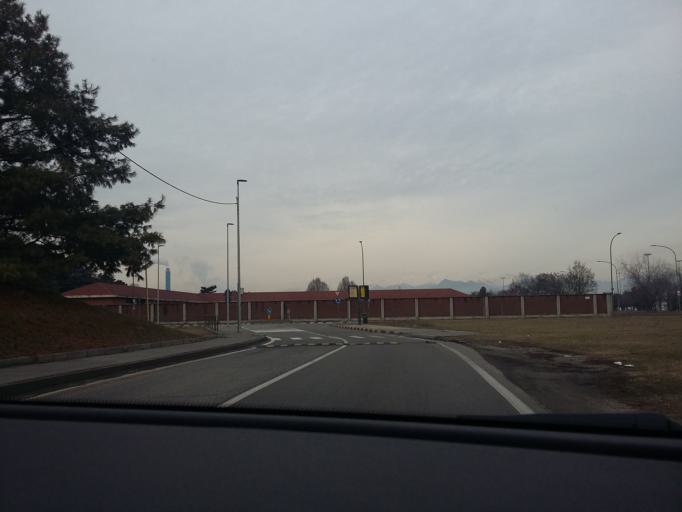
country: IT
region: Piedmont
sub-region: Provincia di Torino
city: Fornaci
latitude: 45.0339
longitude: 7.6063
